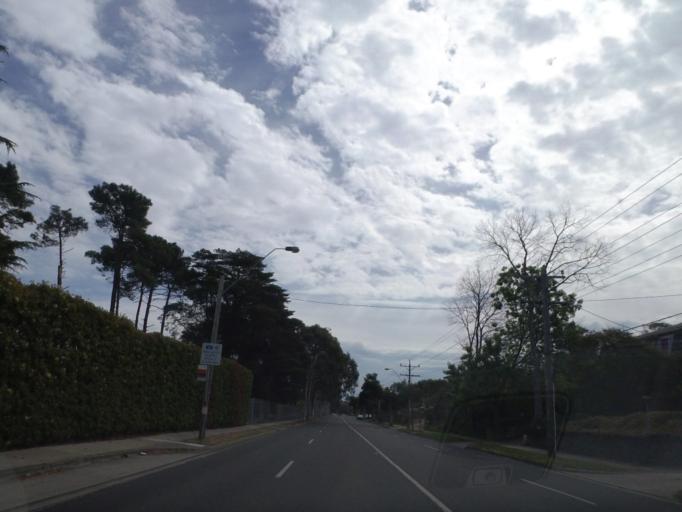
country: AU
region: Victoria
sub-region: Monash
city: Ashwood
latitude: -37.8685
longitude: 145.1157
